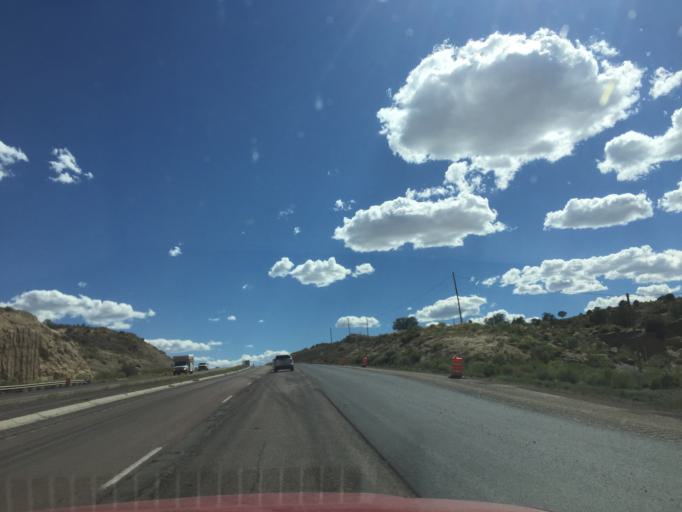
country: US
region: New Mexico
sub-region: McKinley County
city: Twin Lakes
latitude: 35.6504
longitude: -108.7704
